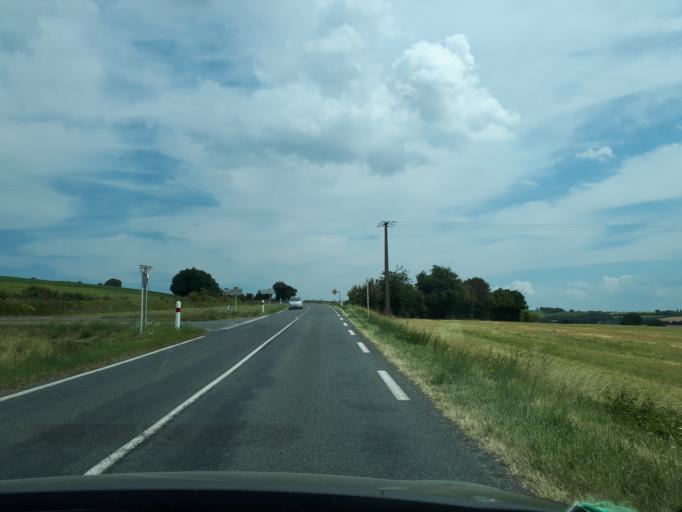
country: FR
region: Centre
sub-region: Departement du Cher
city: Rians
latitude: 47.2343
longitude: 2.6446
